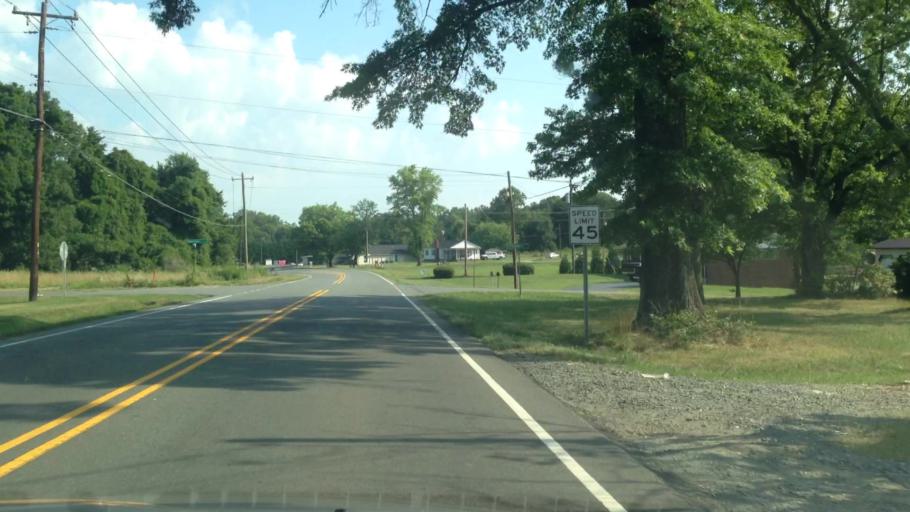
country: US
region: North Carolina
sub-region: Forsyth County
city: Walkertown
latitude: 36.1504
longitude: -80.1277
